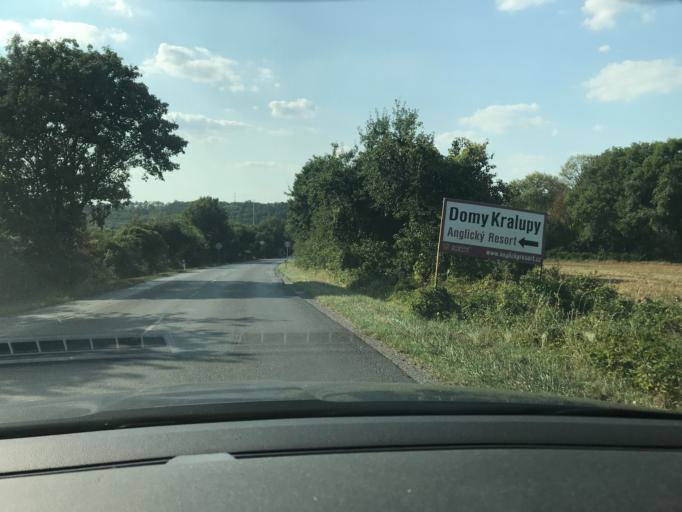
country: CZ
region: Central Bohemia
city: Kralupy nad Vltavou
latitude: 50.2180
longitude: 14.3036
